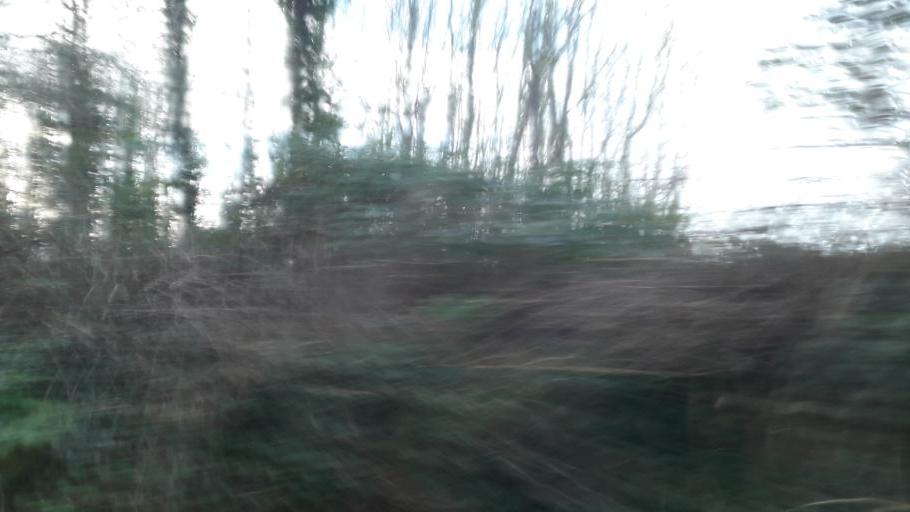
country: IE
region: Leinster
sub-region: Fingal County
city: Skerries
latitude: 53.5709
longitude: -6.1324
